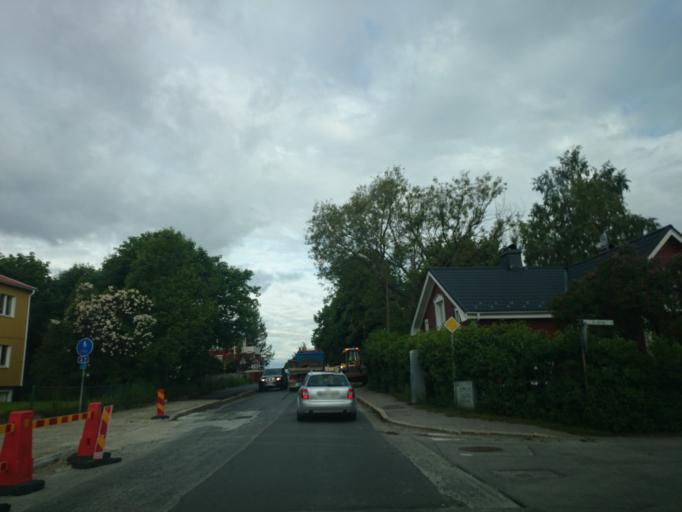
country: SE
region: Vaesternorrland
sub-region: Sundsvalls Kommun
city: Sundsvall
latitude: 62.3801
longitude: 17.3345
